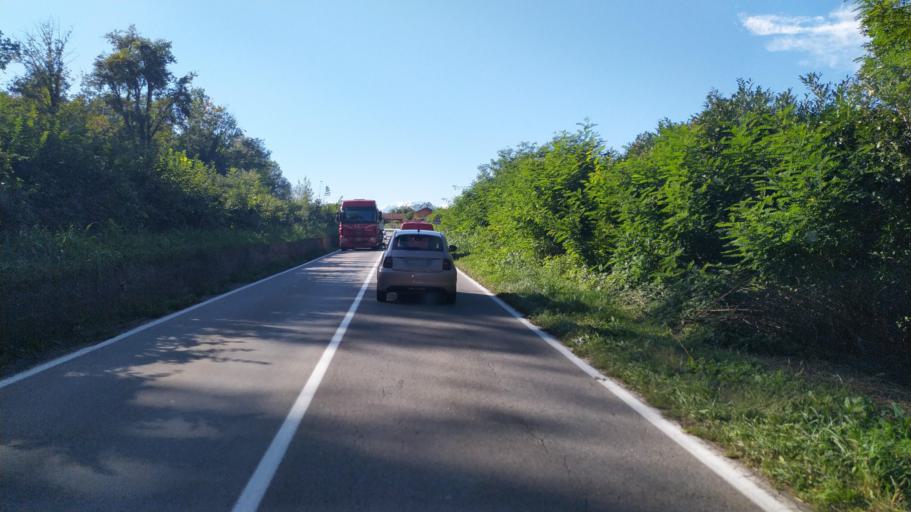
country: IT
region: Lombardy
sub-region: Provincia di Varese
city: Galliate Lombardo
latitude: 45.7903
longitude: 8.7685
